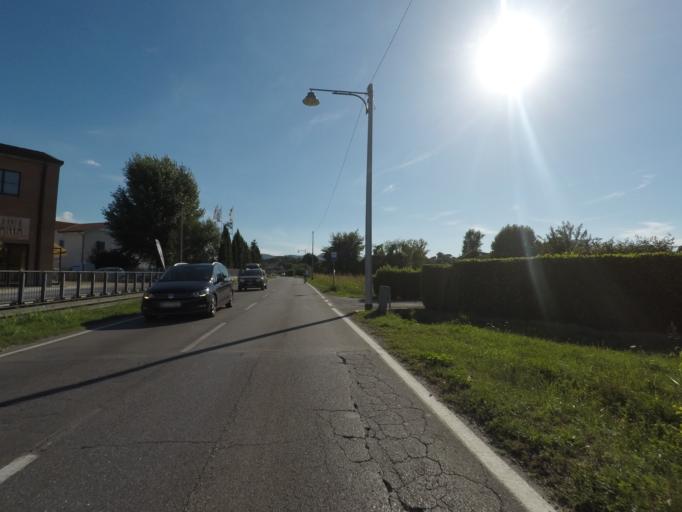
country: IT
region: Tuscany
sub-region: Provincia di Lucca
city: Lucca
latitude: 43.8680
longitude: 10.5120
